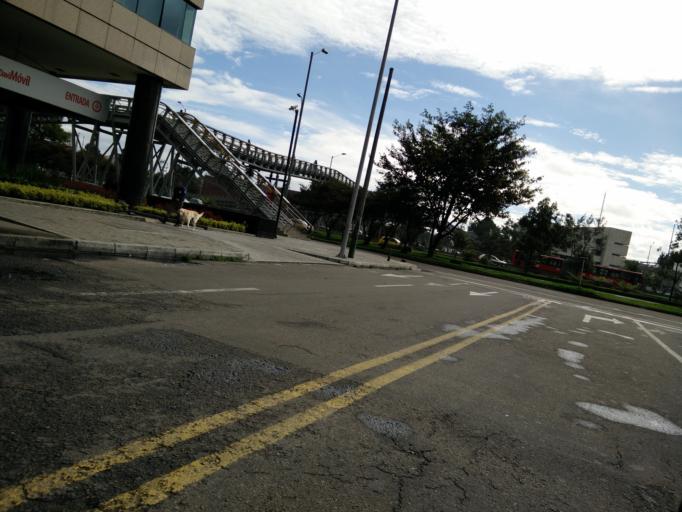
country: CO
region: Bogota D.C.
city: Bogota
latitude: 4.6553
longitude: -74.1056
